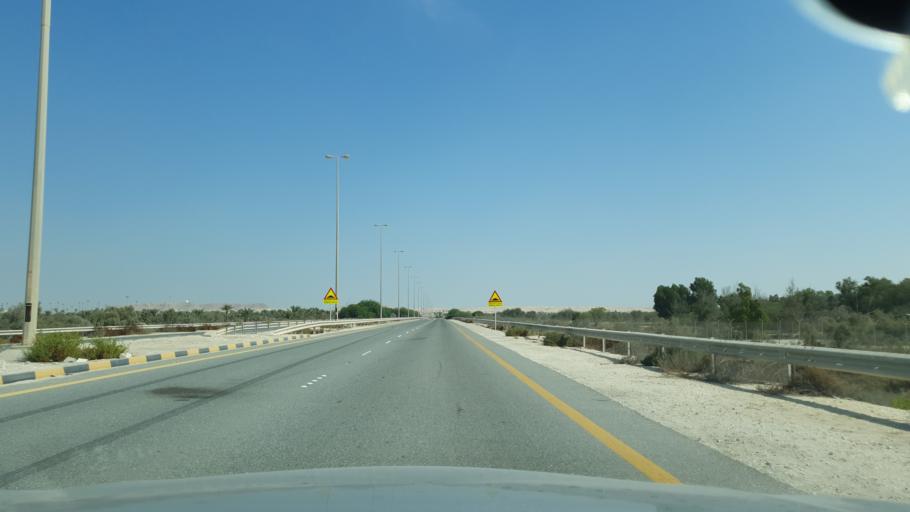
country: BH
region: Central Governorate
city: Dar Kulayb
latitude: 26.0190
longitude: 50.4952
